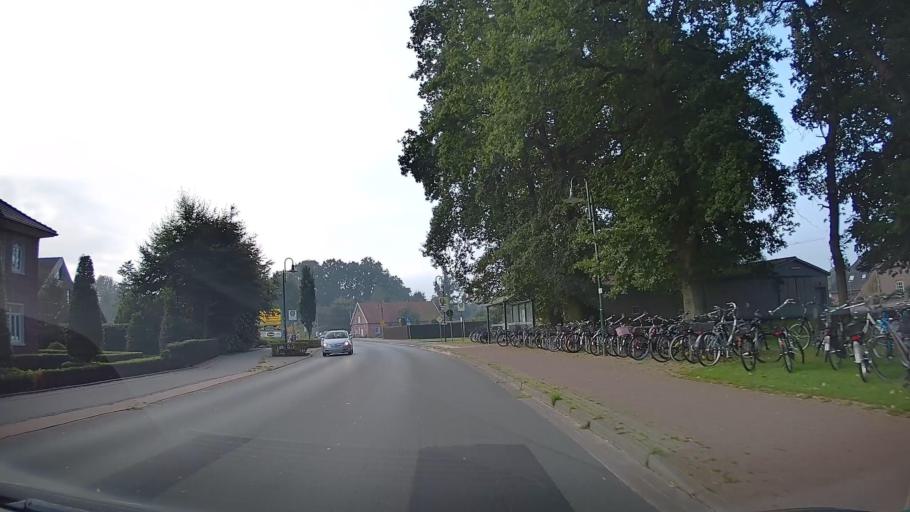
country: DE
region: Lower Saxony
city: Garrel
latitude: 52.9613
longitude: 8.0262
